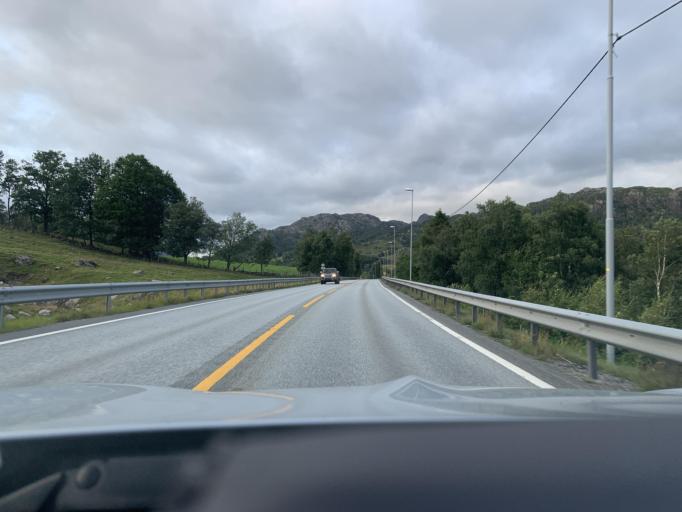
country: NO
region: Rogaland
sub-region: Bjerkreim
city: Vikesa
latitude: 58.6074
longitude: 6.0857
